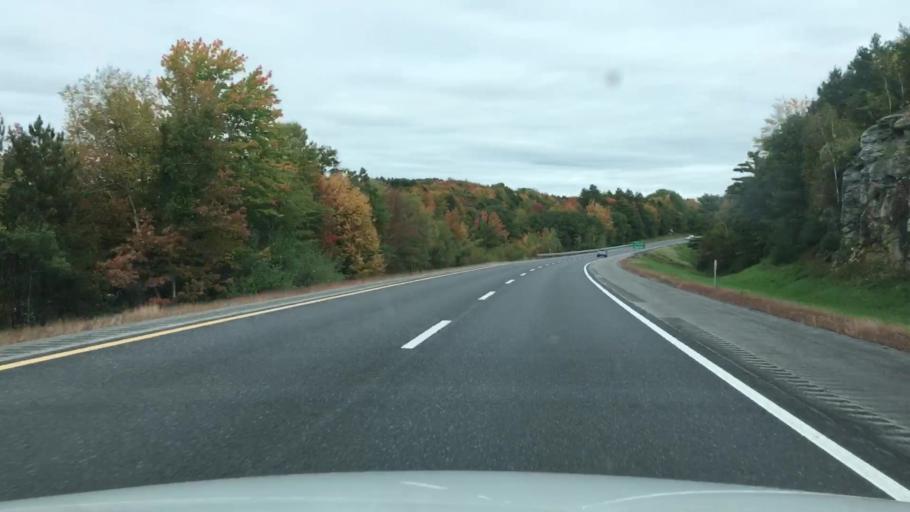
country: US
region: Maine
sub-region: Sagadahoc County
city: Topsham
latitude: 43.9913
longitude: -69.9389
